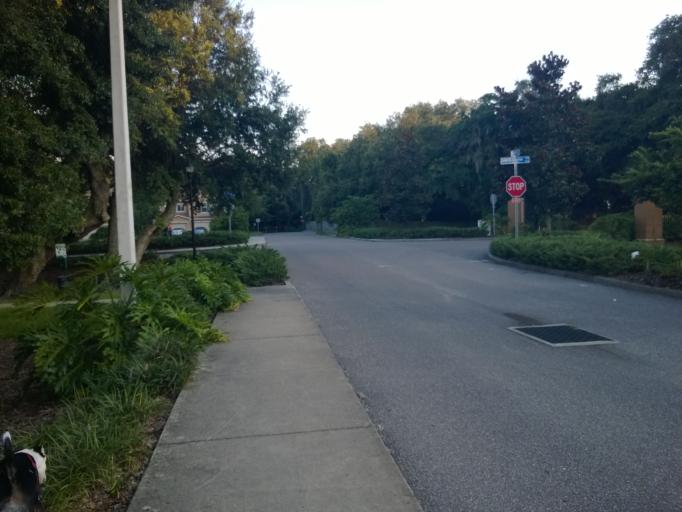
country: US
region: Florida
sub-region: Hillsborough County
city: Riverview
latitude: 27.8801
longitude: -82.3255
